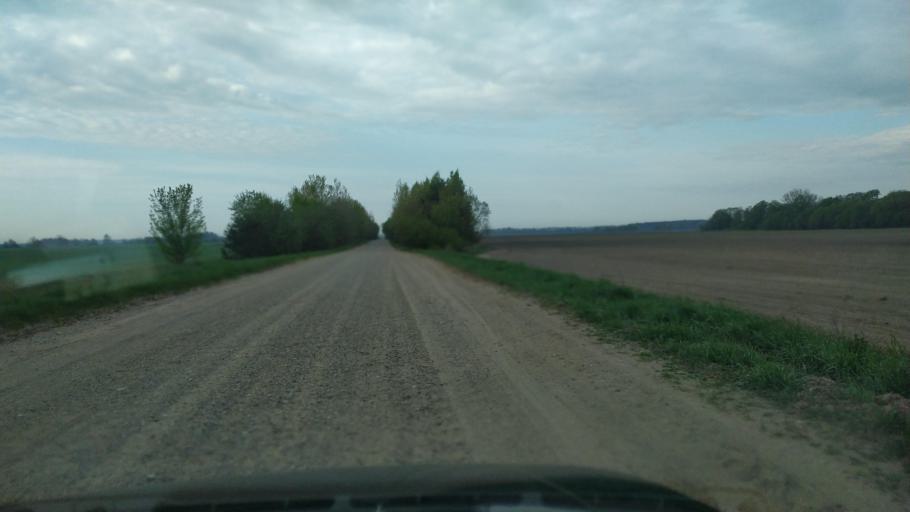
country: BY
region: Brest
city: Zhabinka
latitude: 52.1434
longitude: 24.0929
